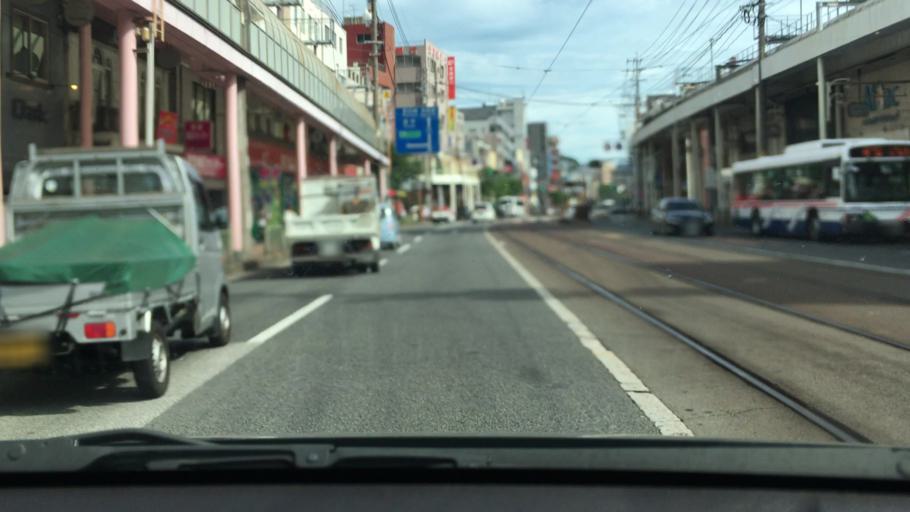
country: JP
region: Nagasaki
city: Obita
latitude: 32.7914
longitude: 129.8603
